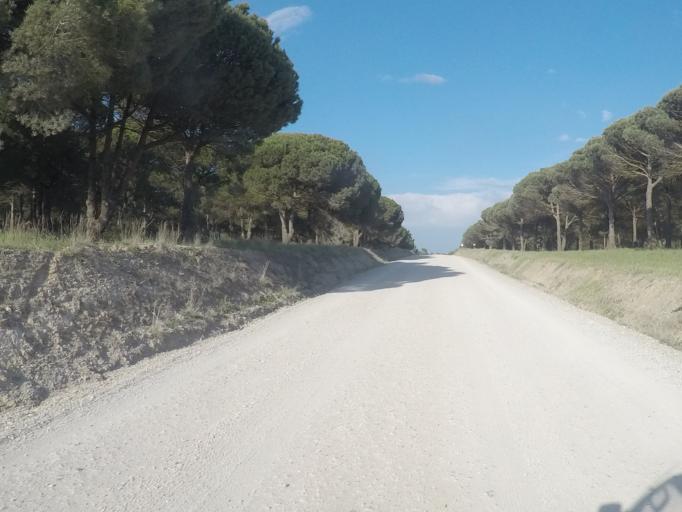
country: PT
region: Setubal
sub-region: Sesimbra
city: Sesimbra
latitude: 38.4533
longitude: -9.1941
